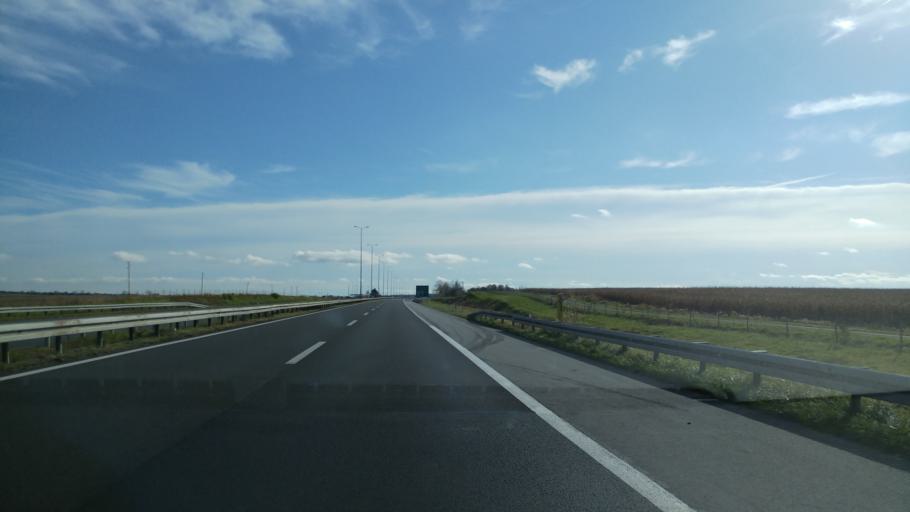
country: HR
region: Sisacko-Moslavacka
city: Lipovljani
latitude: 45.4089
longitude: 16.8553
